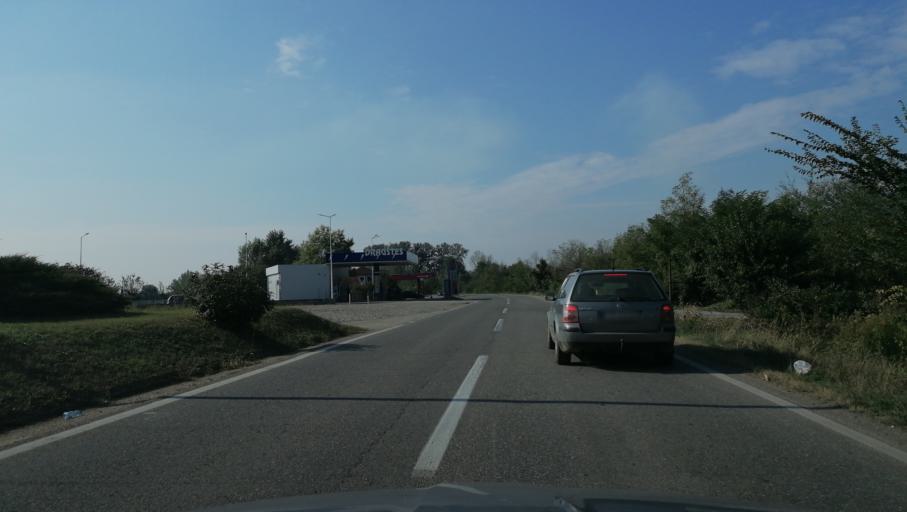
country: BA
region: Republika Srpska
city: Popovi
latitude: 44.7794
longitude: 19.3182
